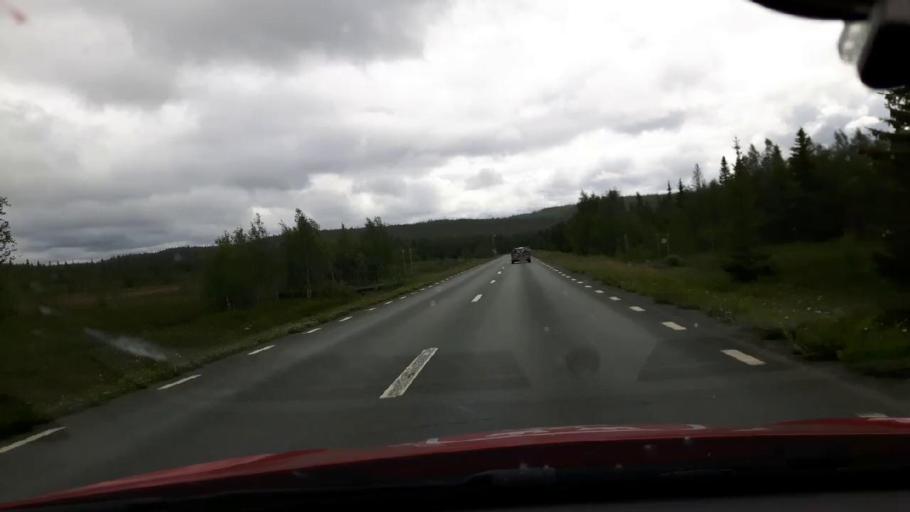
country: SE
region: Jaemtland
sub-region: Are Kommun
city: Are
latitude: 63.3683
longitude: 12.7031
